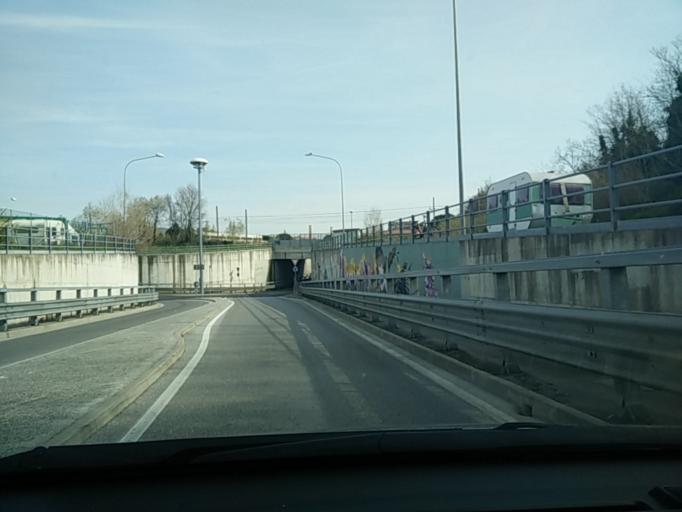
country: IT
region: Emilia-Romagna
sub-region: Provincia di Rimini
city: Rimini
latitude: 44.0716
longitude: 12.5406
